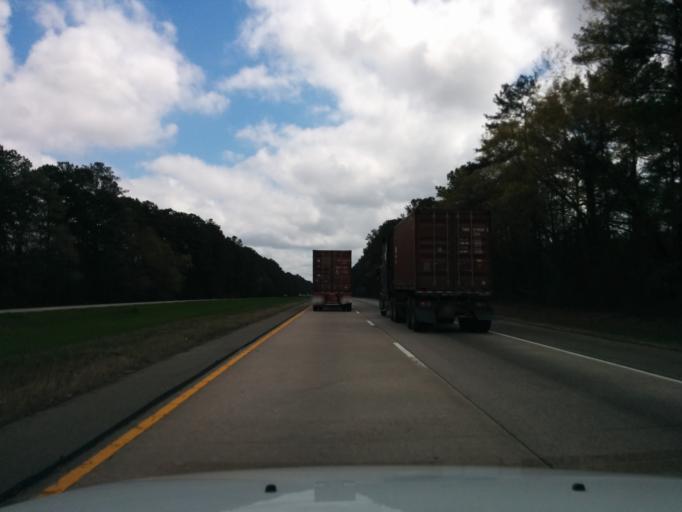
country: US
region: Georgia
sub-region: Bryan County
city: Pembroke
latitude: 32.1945
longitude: -81.4779
